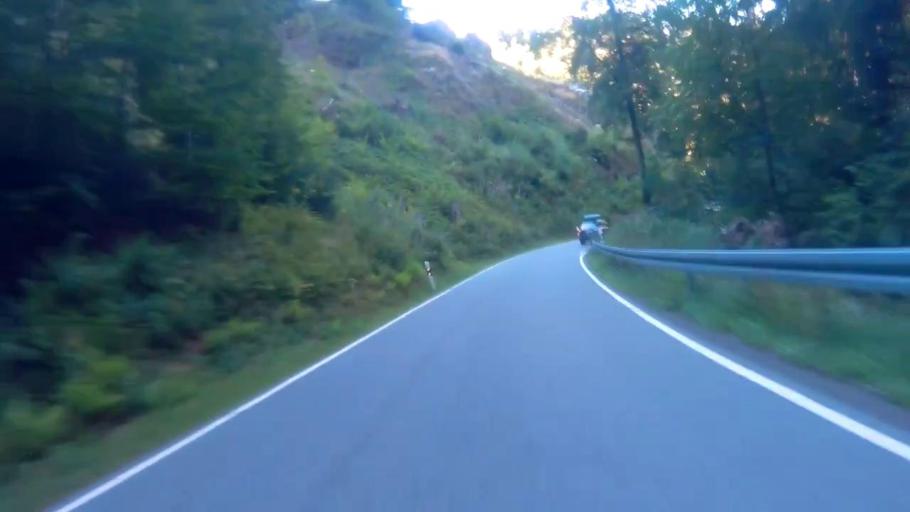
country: DE
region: Baden-Wuerttemberg
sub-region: Freiburg Region
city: Horben
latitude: 47.8899
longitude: 7.8609
